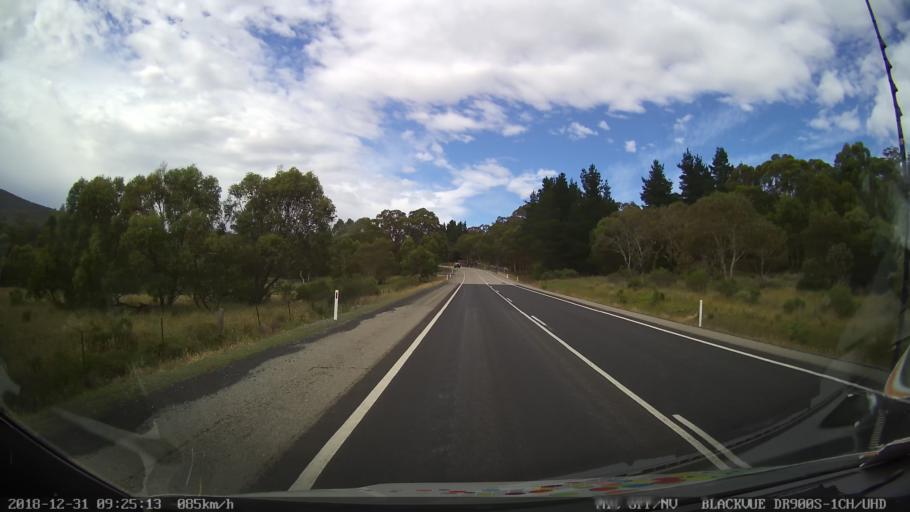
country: AU
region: New South Wales
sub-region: Snowy River
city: Jindabyne
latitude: -36.4418
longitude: 148.5099
